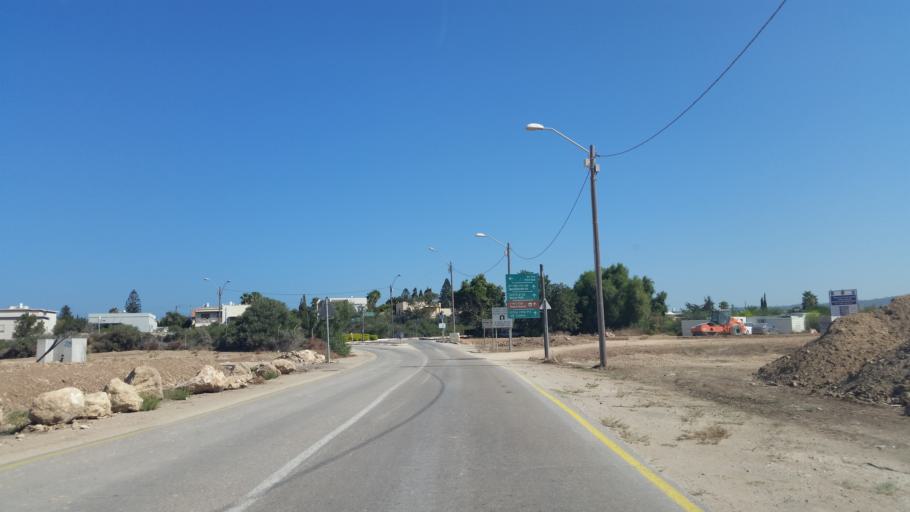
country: IL
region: Haifa
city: `Atlit
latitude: 32.6793
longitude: 34.9343
